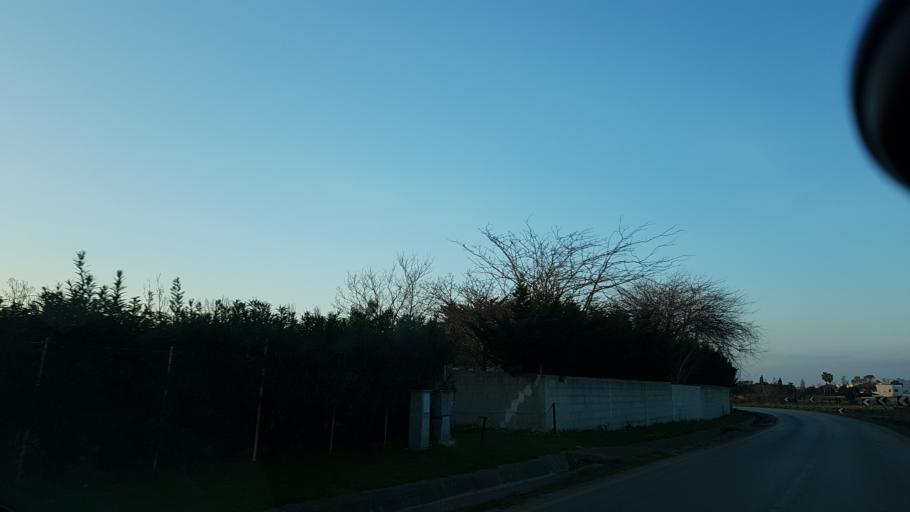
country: IT
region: Apulia
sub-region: Provincia di Brindisi
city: La Rosa
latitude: 40.6036
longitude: 17.9461
